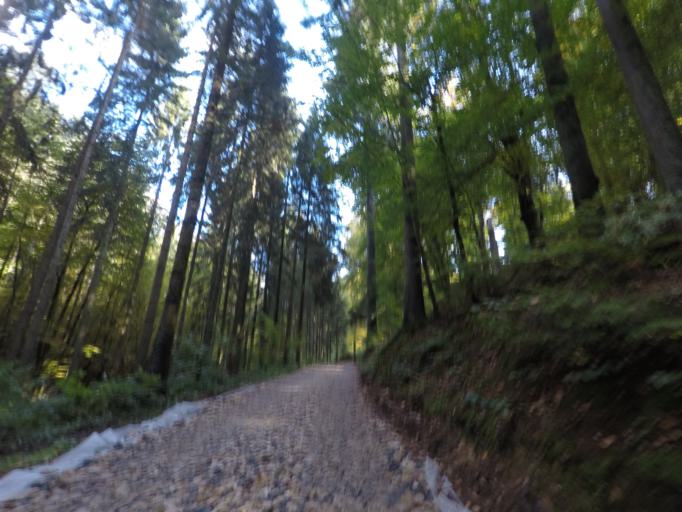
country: LU
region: Luxembourg
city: Itzig
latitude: 49.6069
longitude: 6.1798
